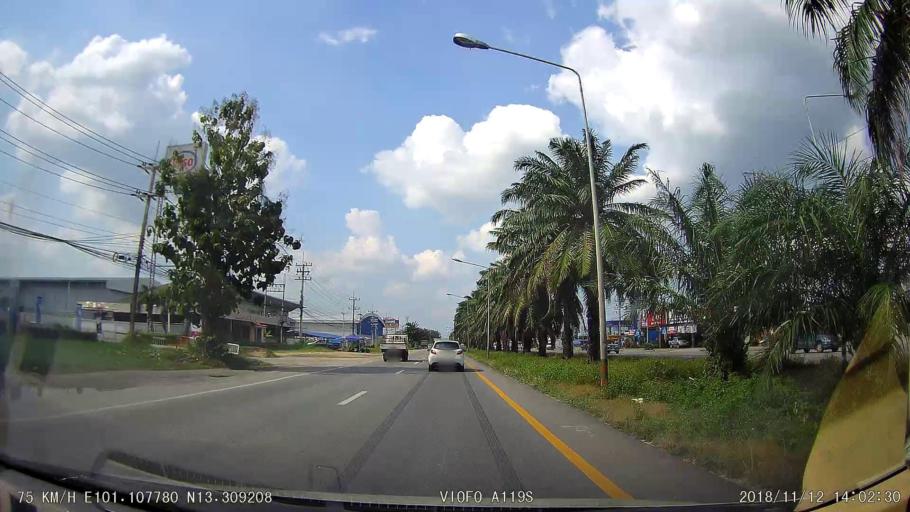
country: TH
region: Chon Buri
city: Ban Bueng
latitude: 13.3120
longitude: 101.1063
